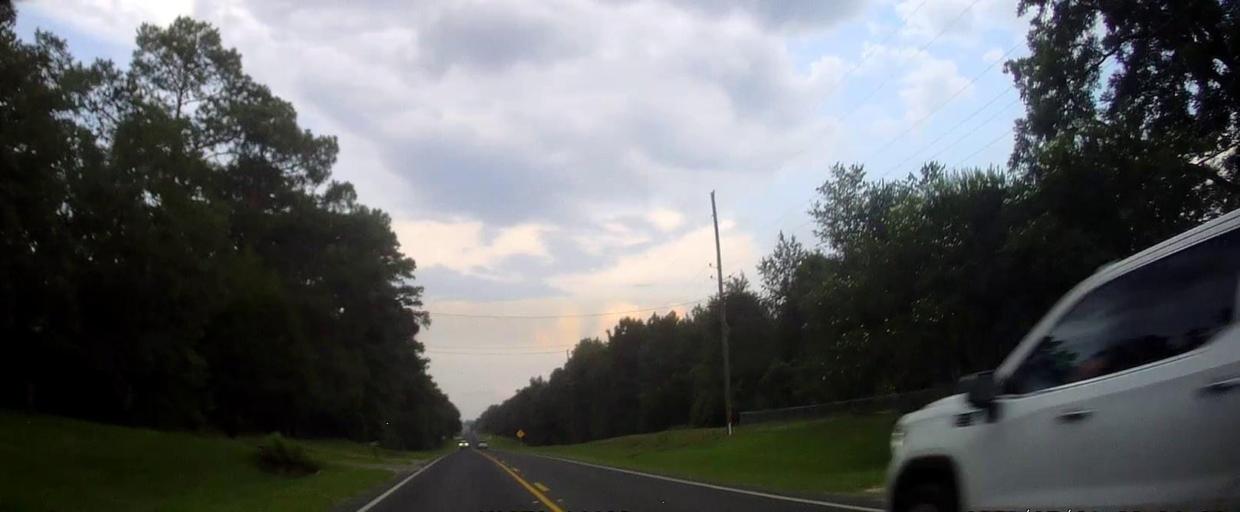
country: US
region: Georgia
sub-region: Laurens County
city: East Dublin
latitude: 32.5363
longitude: -82.8458
